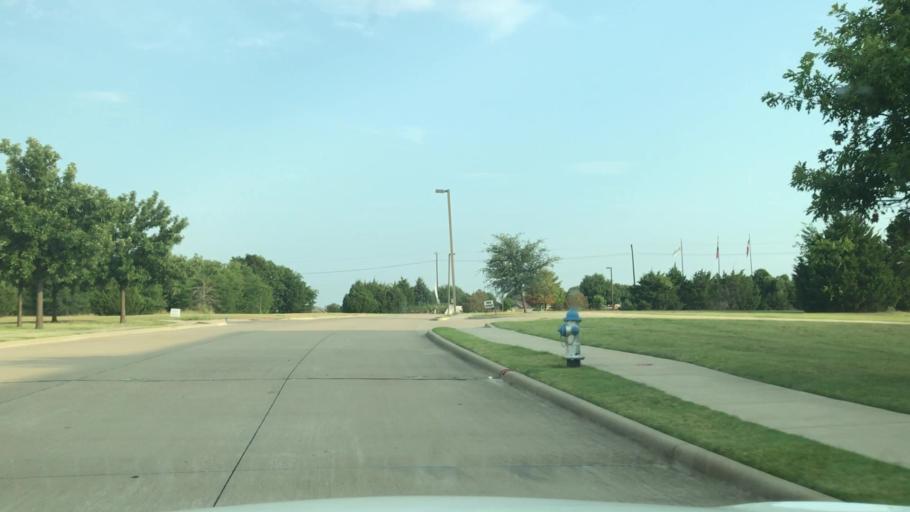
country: US
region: Texas
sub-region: Rockwall County
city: Rockwall
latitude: 32.9082
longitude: -96.4240
